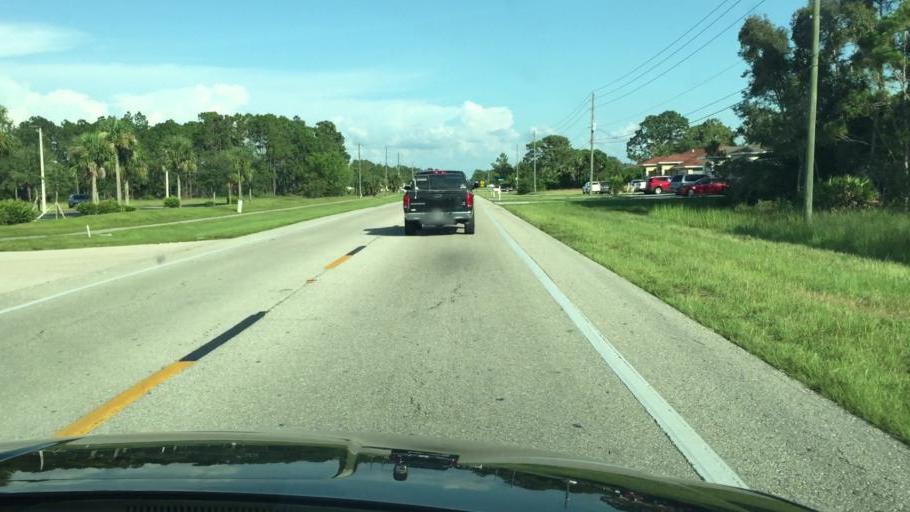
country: US
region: Florida
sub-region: Lee County
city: Gateway
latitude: 26.6103
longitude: -81.7460
